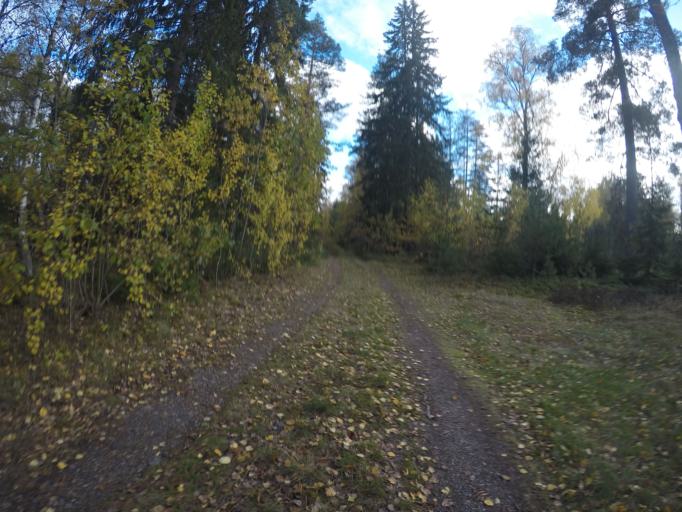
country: SE
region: Vaestmanland
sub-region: Arboga Kommun
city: Tyringe
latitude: 59.3532
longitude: 15.9574
